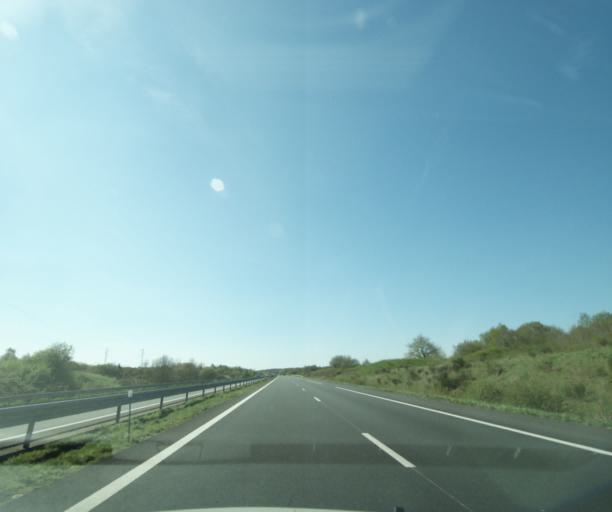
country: FR
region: Centre
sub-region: Departement du Loir-et-Cher
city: Theillay
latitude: 47.3058
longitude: 2.0472
